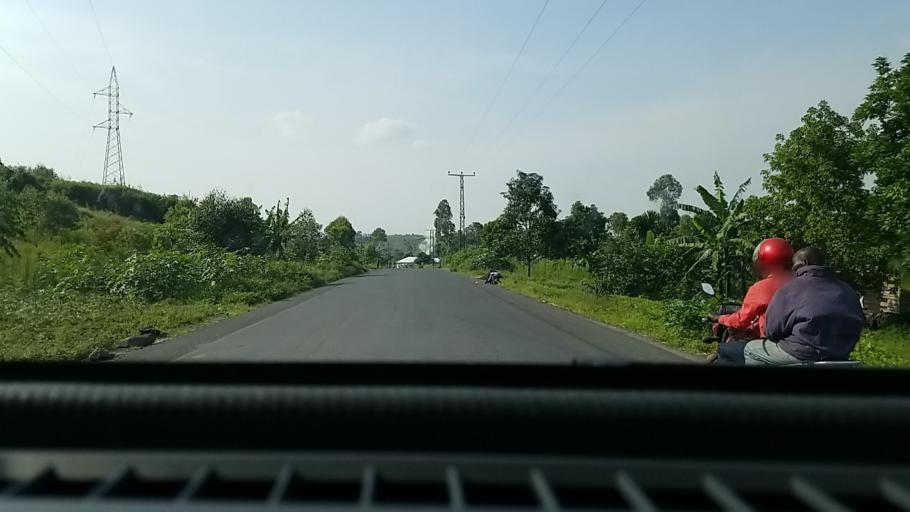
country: CD
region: Nord Kivu
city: Sake
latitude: -1.6113
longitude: 29.1403
